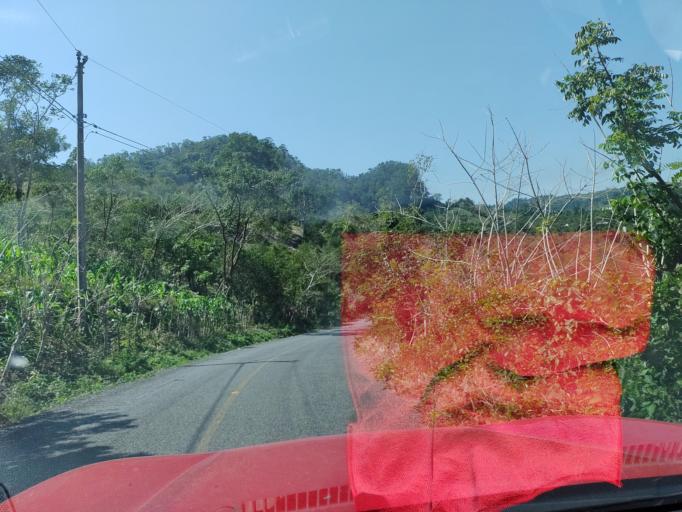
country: MX
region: Veracruz
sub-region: Papantla
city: Polutla
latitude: 20.4997
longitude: -97.2187
